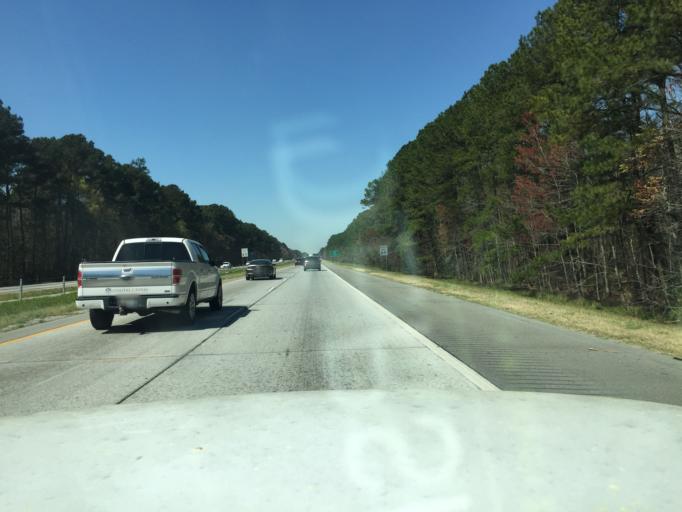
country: US
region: Georgia
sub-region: Chatham County
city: Garden City
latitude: 32.0679
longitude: -81.1779
